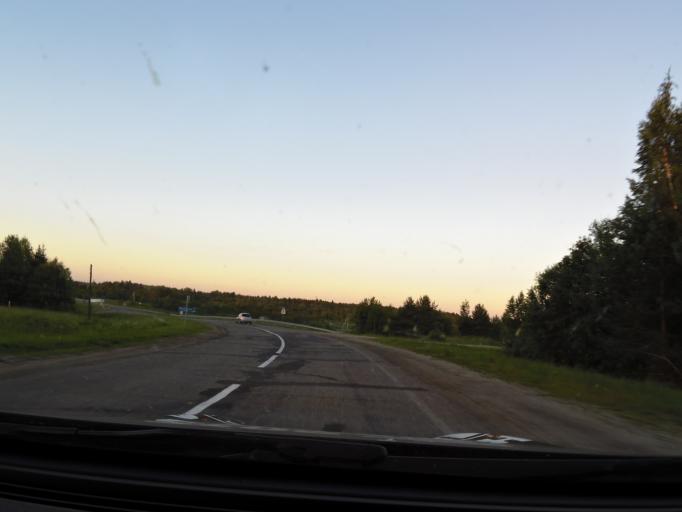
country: RU
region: Jaroslavl
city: Lyubim
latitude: 58.3501
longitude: 40.7888
